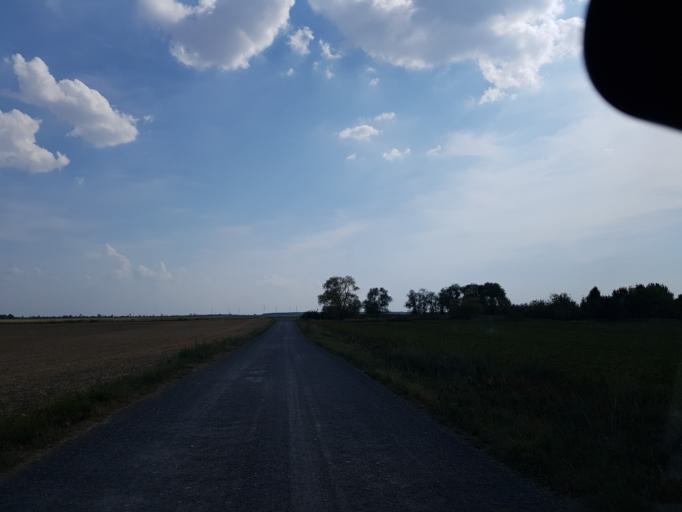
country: DE
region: Brandenburg
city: Treuenbrietzen
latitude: 51.9920
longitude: 12.8686
